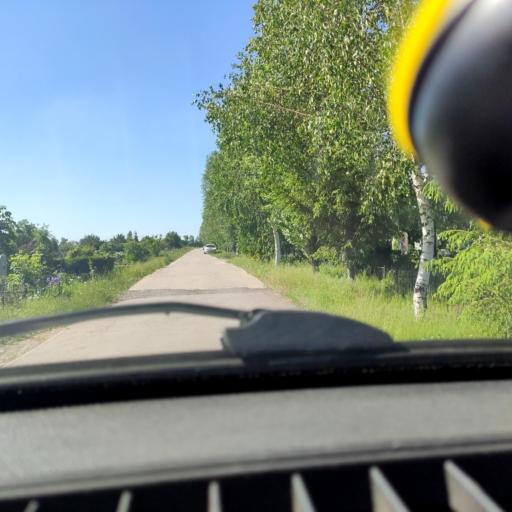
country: RU
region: Samara
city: Tol'yatti
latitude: 53.5740
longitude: 49.4274
